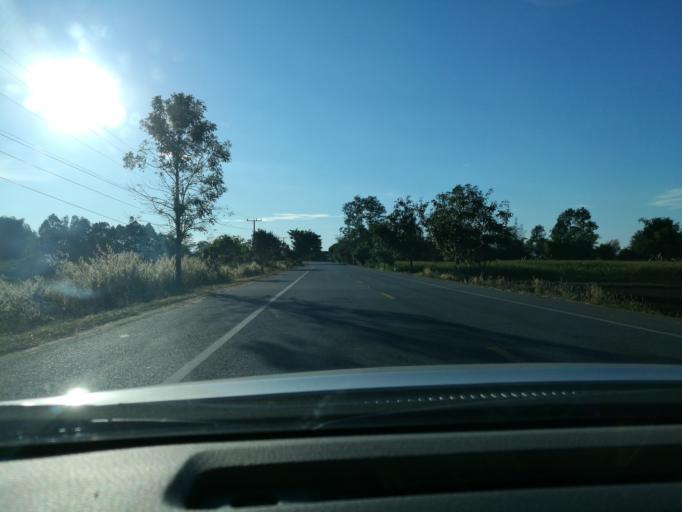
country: TH
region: Phitsanulok
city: Nakhon Thai
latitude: 17.0741
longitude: 100.8306
